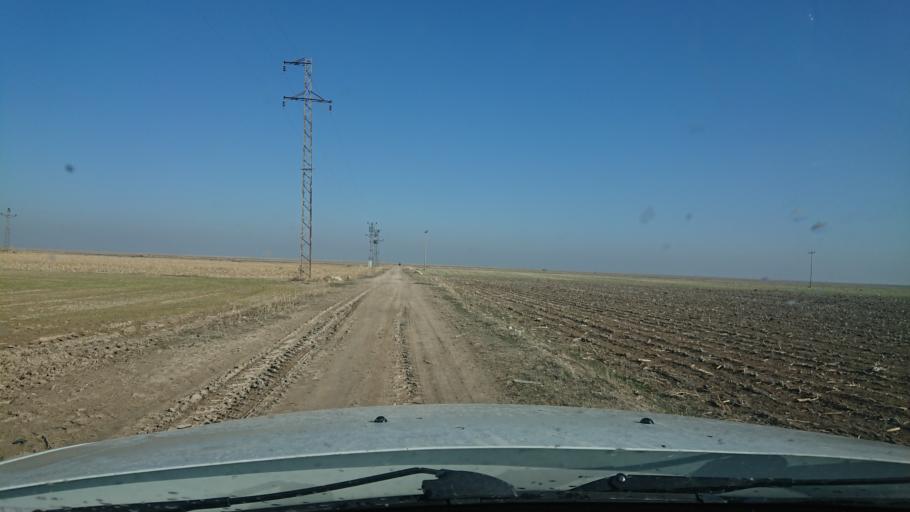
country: TR
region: Aksaray
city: Sultanhani
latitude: 38.3102
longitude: 33.5218
